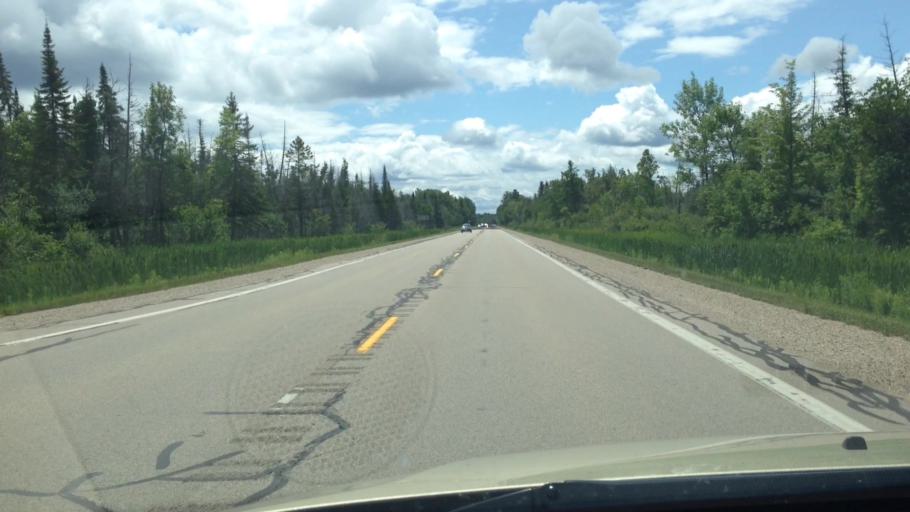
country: US
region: Michigan
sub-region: Menominee County
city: Menominee
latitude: 45.3945
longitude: -87.3681
